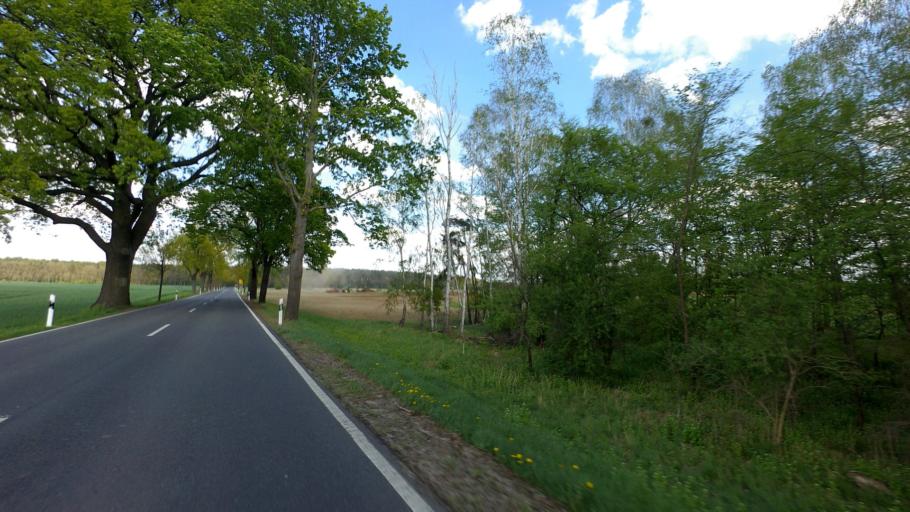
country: DE
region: Brandenburg
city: Marienwerder
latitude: 52.8756
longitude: 13.5414
